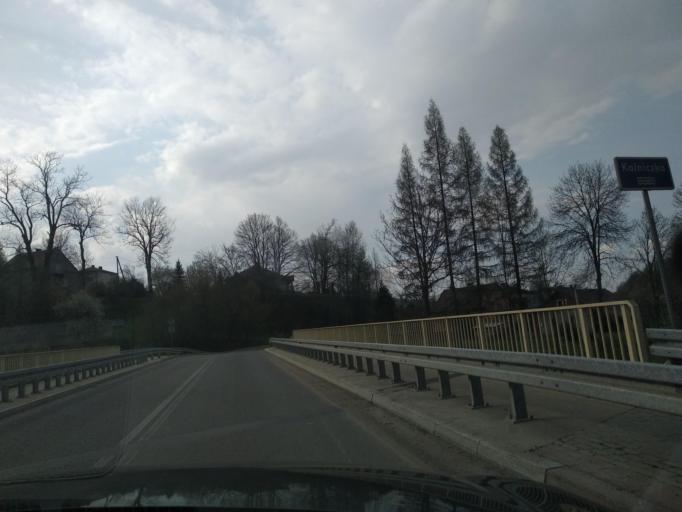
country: PL
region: Subcarpathian Voivodeship
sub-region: Powiat sanocki
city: Czaszyn
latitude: 49.4572
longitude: 22.2560
